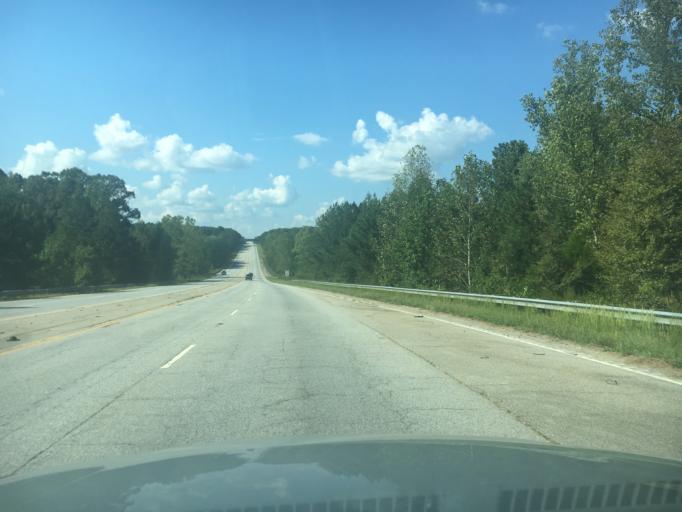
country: US
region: South Carolina
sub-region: Greenwood County
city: Ware Shoals
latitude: 34.4048
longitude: -82.2239
